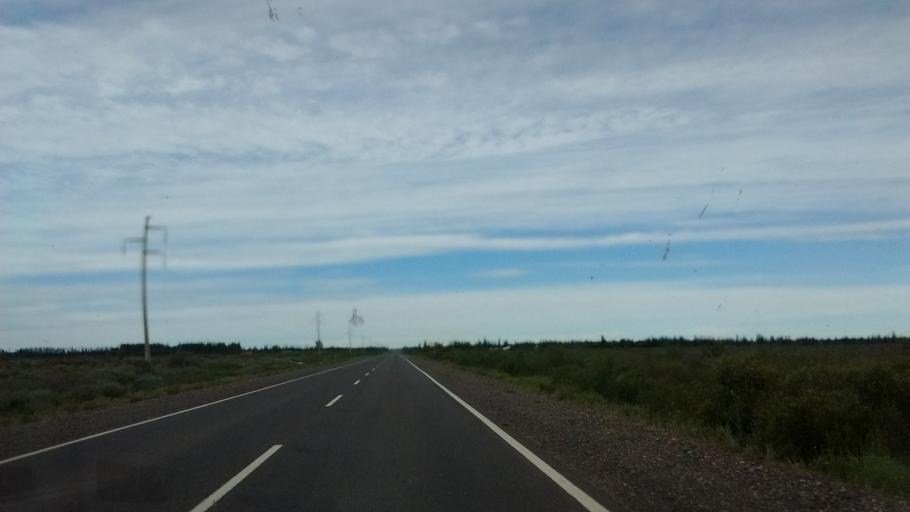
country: AR
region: Rio Negro
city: Contraalmirante Cordero
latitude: -38.6555
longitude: -68.1408
